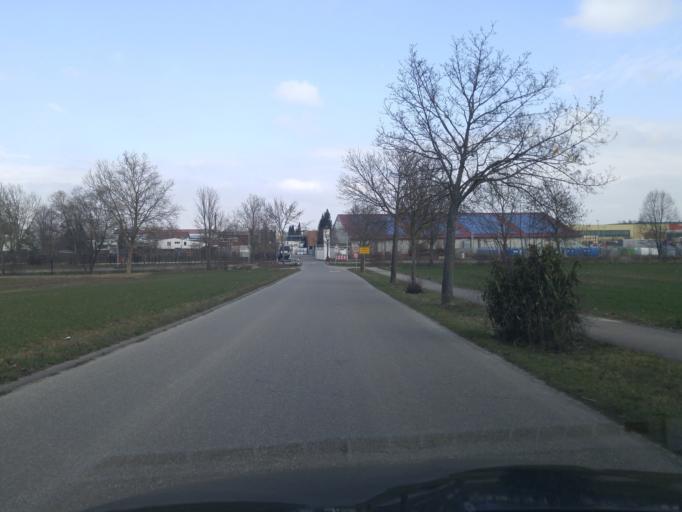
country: DE
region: Baden-Wuerttemberg
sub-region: Regierungsbezirk Stuttgart
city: Ilsfeld
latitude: 49.0537
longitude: 9.2614
